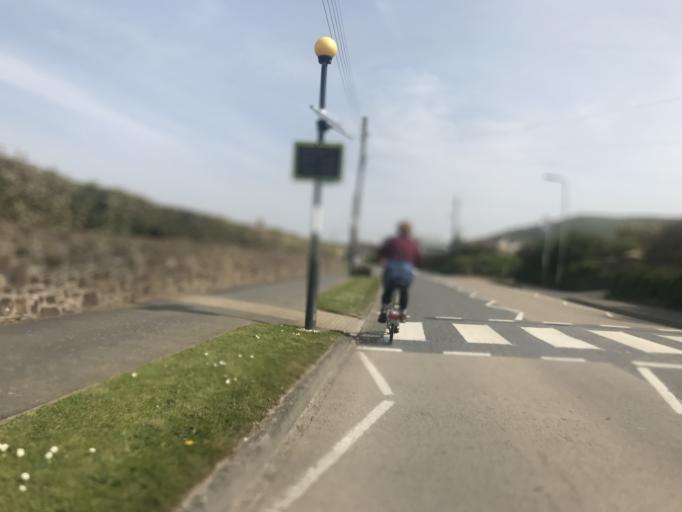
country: GB
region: England
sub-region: Devon
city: Braunton
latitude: 51.1267
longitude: -4.2340
